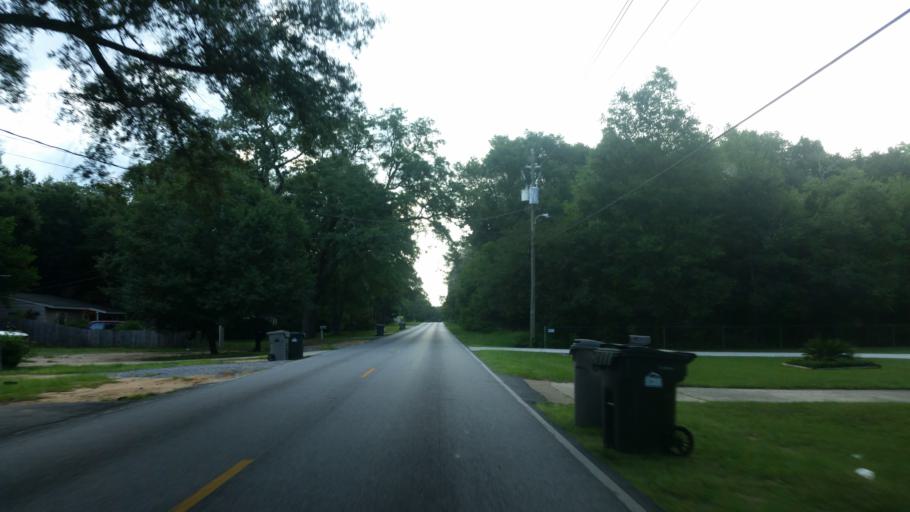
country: US
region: Florida
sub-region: Escambia County
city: Bellview
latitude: 30.4490
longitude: -87.3098
